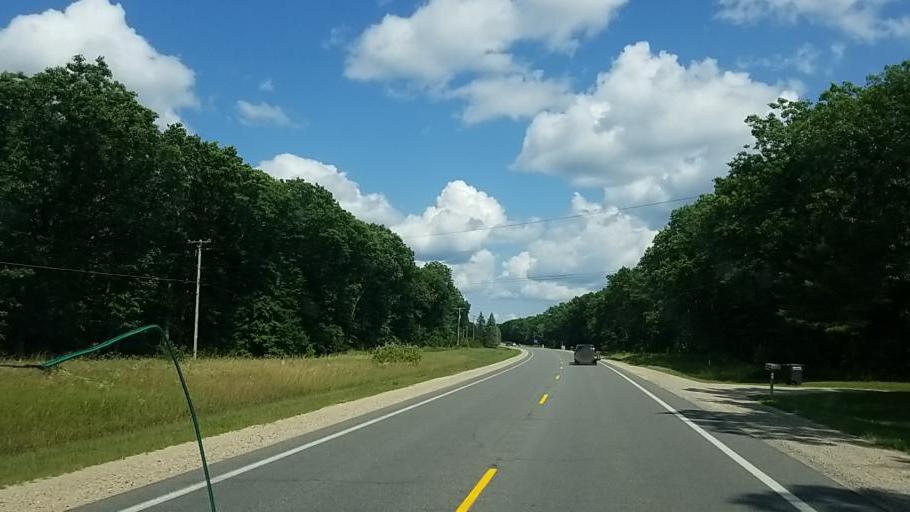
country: US
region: Michigan
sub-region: Newaygo County
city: Newaygo
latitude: 43.4044
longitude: -85.7363
